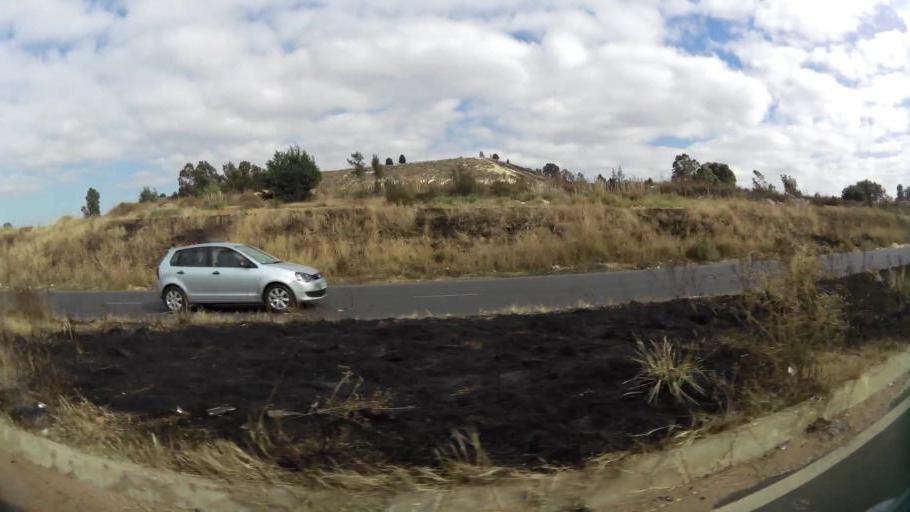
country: ZA
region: Gauteng
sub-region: City of Johannesburg Metropolitan Municipality
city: Roodepoort
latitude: -26.2048
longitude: 27.9046
